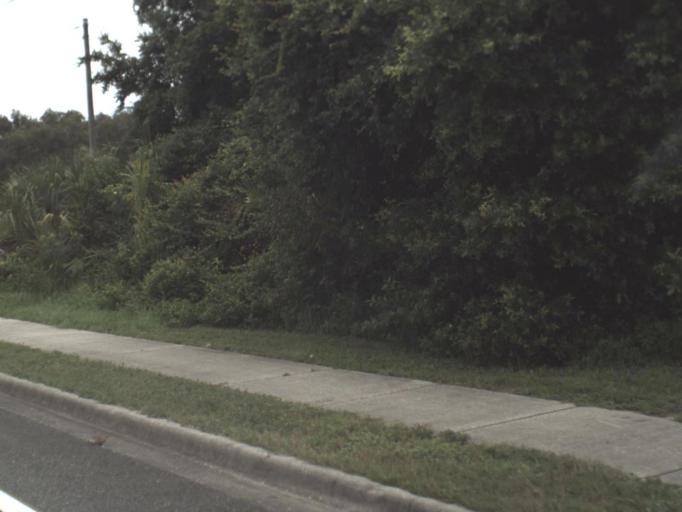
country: US
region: Florida
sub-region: Citrus County
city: Inverness
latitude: 28.8400
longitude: -82.3068
